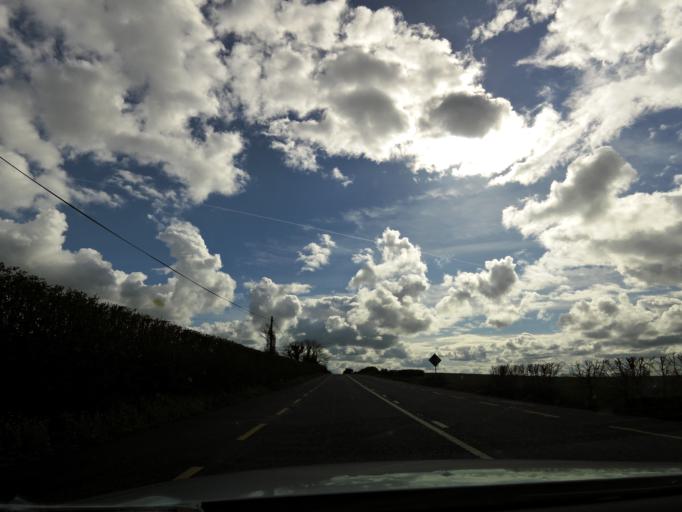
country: IE
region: Leinster
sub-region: Laois
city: Rathdowney
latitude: 52.7876
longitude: -7.5213
